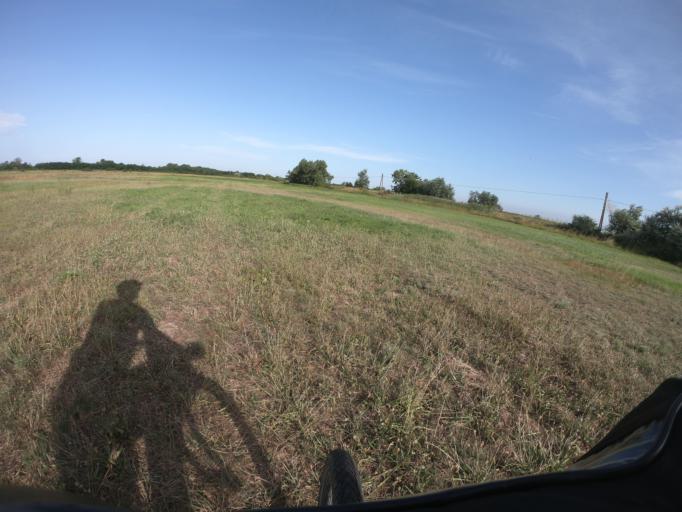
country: HU
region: Hajdu-Bihar
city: Tiszacsege
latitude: 47.6142
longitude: 21.0198
